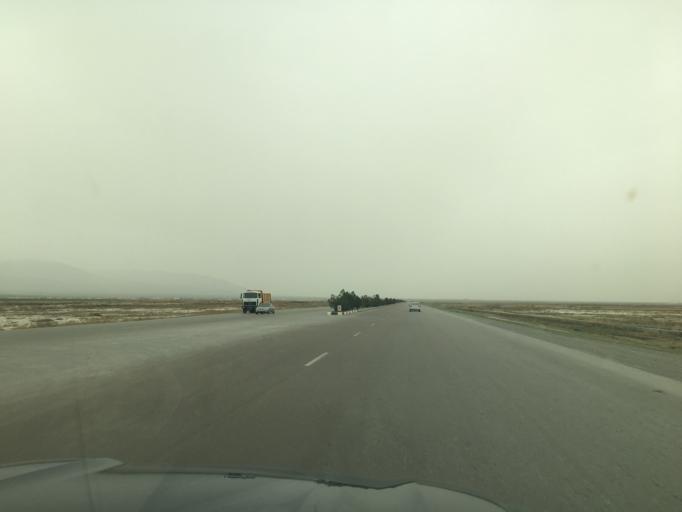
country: TM
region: Ahal
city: Baharly
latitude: 38.3606
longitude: 57.5330
